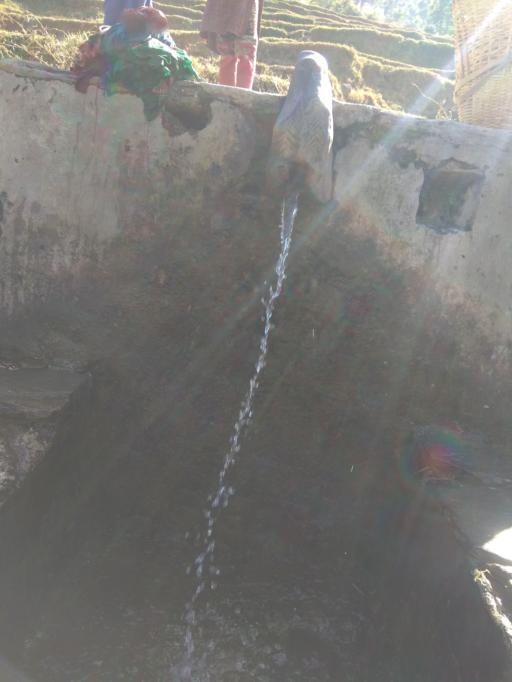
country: NP
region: Far Western
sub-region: Seti Zone
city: Achham
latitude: 29.2405
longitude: 81.6329
